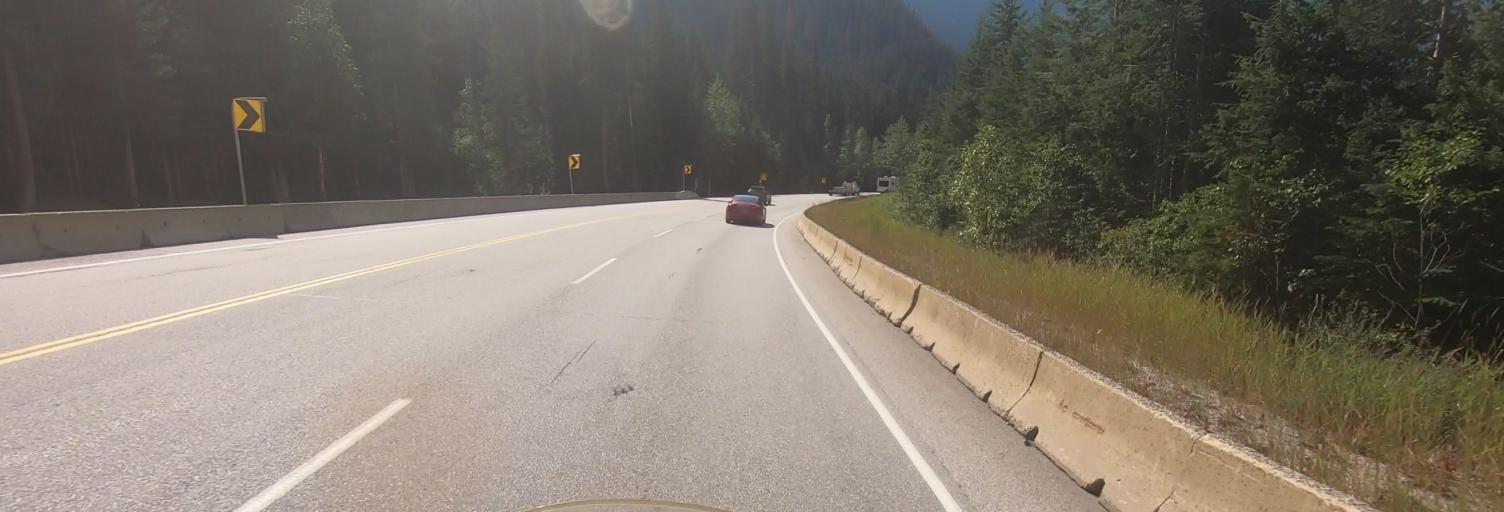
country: CA
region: British Columbia
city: Golden
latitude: 51.3458
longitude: -117.4344
